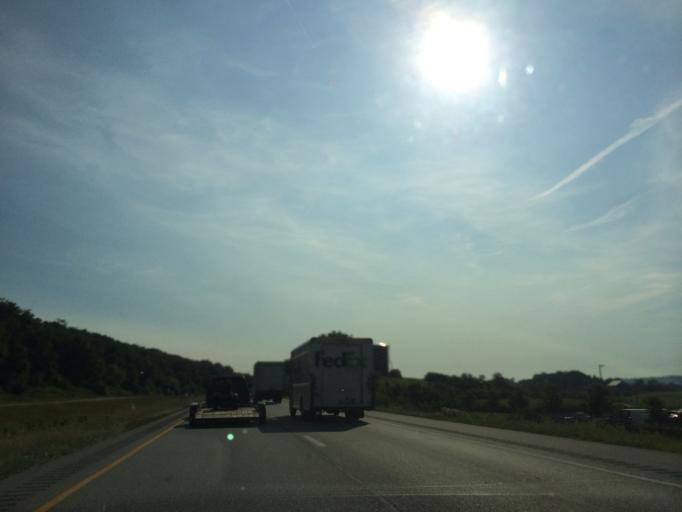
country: US
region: Pennsylvania
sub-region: York County
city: Wrightsville
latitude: 40.0305
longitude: -76.5467
